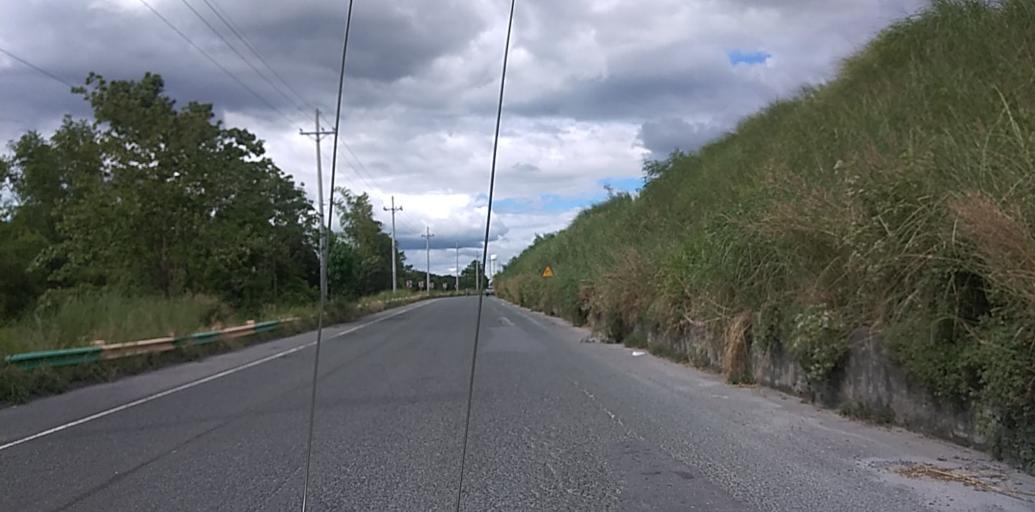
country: PH
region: Central Luzon
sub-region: Province of Pampanga
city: Dolores
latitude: 15.1049
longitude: 120.5215
